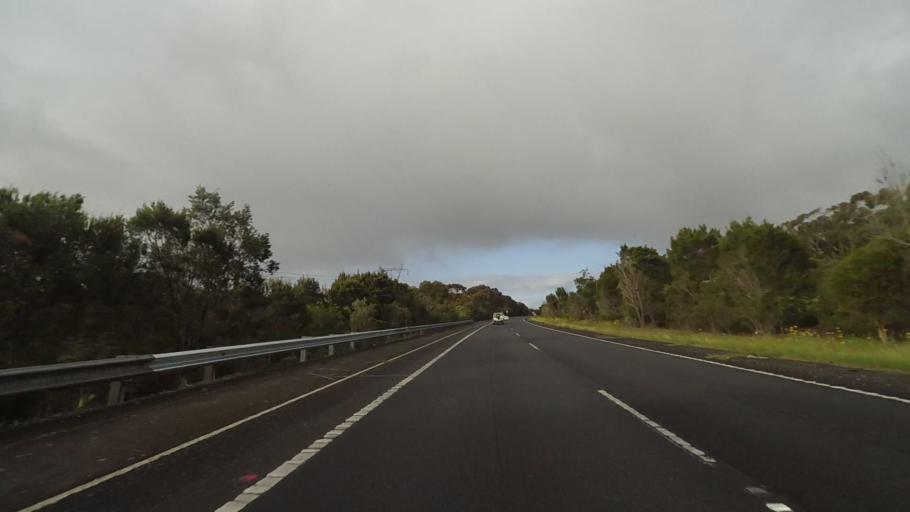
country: AU
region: New South Wales
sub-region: Wollongong
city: Bulli
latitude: -34.2495
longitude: 150.9353
